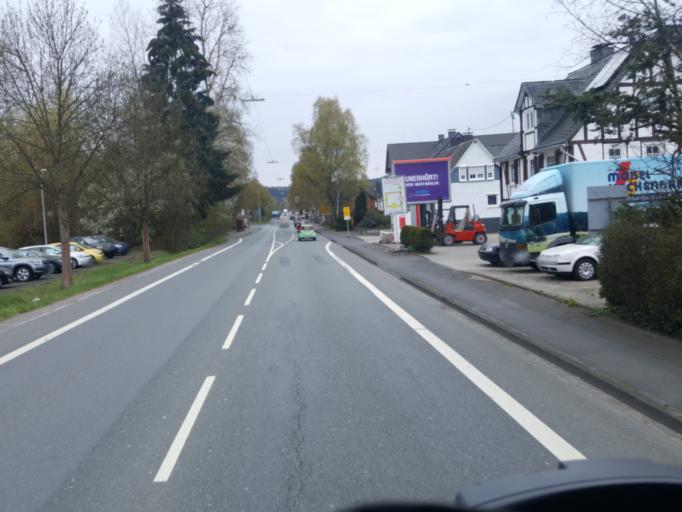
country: DE
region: North Rhine-Westphalia
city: Kreuztal
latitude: 50.9656
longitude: 8.0388
